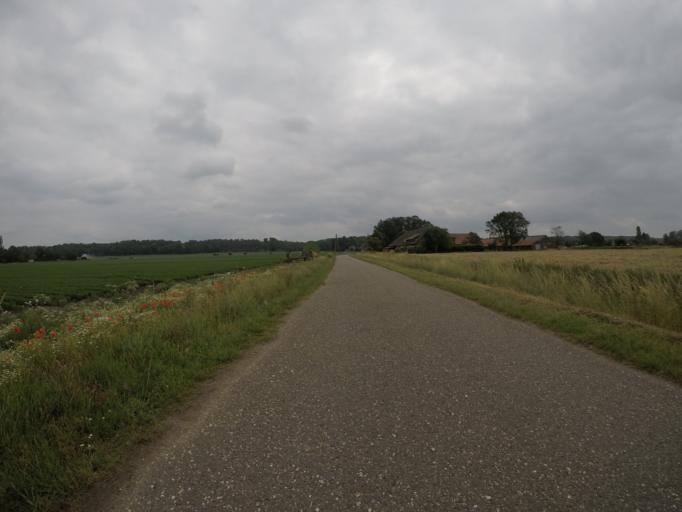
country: DE
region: North Rhine-Westphalia
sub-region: Regierungsbezirk Dusseldorf
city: Hamminkeln
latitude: 51.7399
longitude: 6.6412
